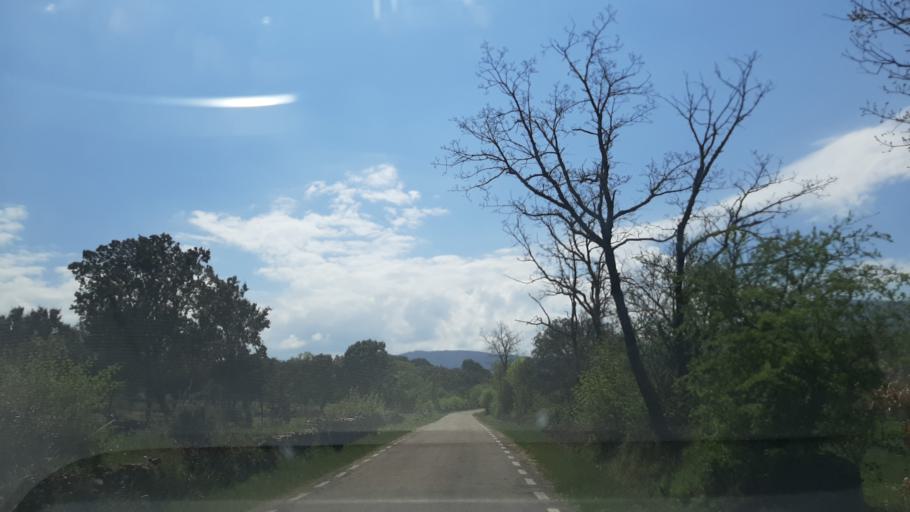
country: ES
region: Castille and Leon
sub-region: Provincia de Salamanca
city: Tejeda y Segoyuela
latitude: 40.6228
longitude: -6.0213
